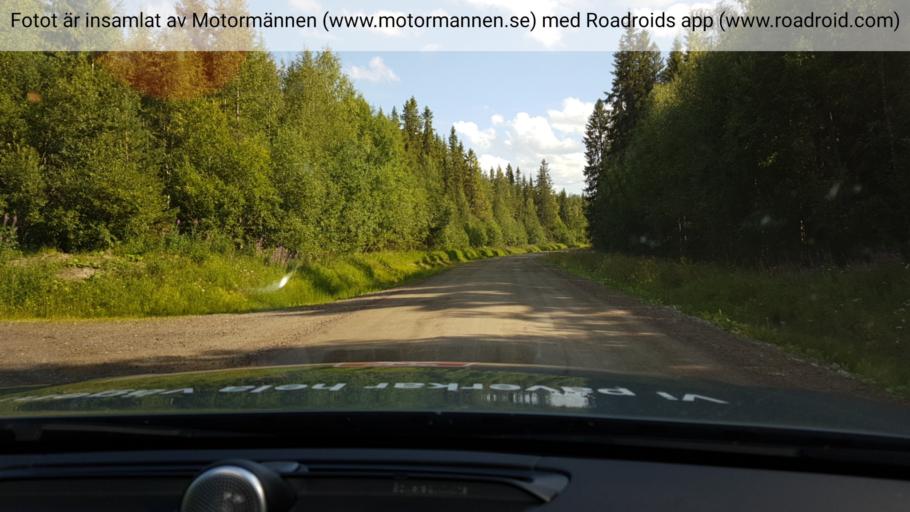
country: SE
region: Jaemtland
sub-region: Stroemsunds Kommun
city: Stroemsund
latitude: 64.0091
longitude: 15.9653
